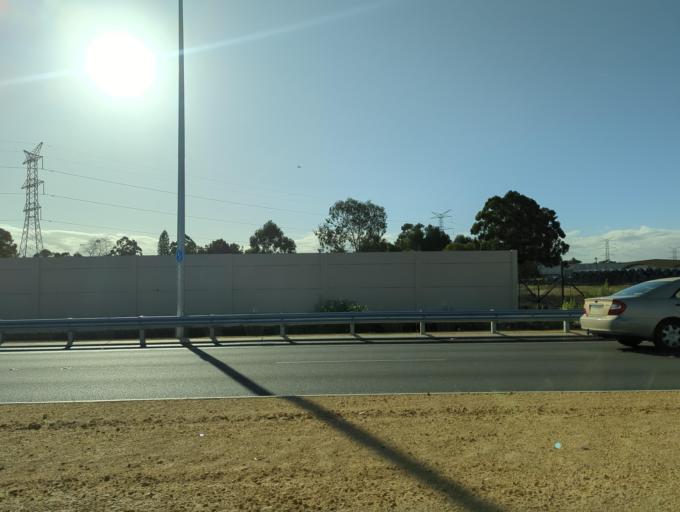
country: AU
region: Western Australia
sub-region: City of Cockburn
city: South Lake
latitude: -32.1157
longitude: 115.8544
